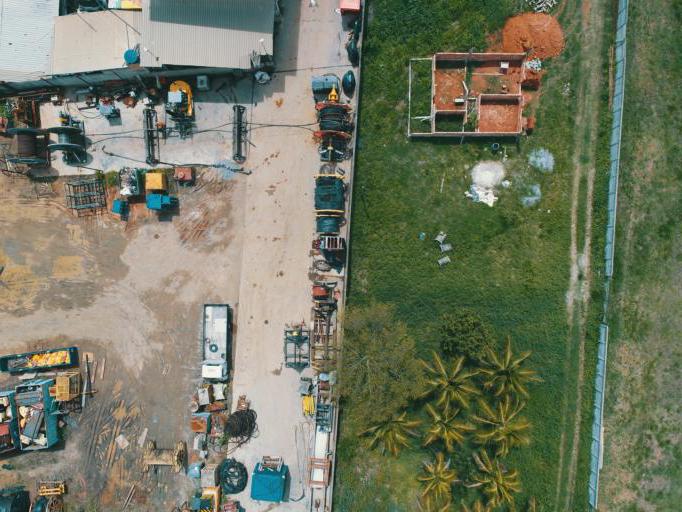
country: BR
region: Rio de Janeiro
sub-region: Macae
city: Macae
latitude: -22.4387
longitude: -41.8697
